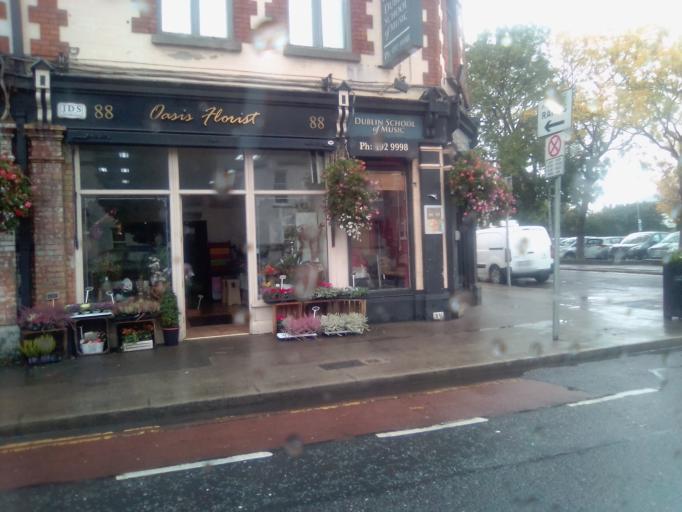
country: IE
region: Leinster
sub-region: South Dublin
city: Terenure
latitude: 53.3115
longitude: -6.2829
